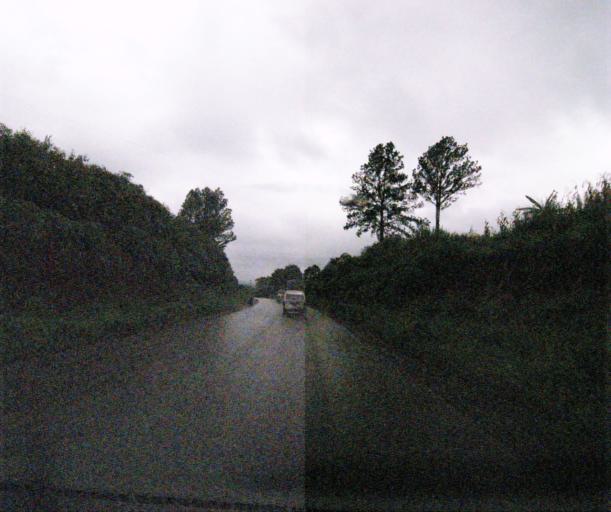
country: CM
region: West
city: Bansoa
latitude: 5.4960
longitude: 10.2550
